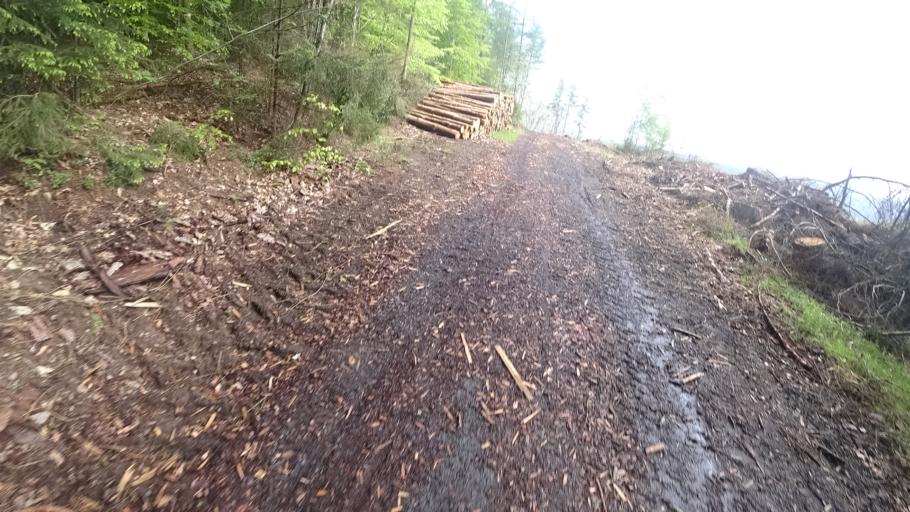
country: DE
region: Rheinland-Pfalz
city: Alsdorf
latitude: 50.7786
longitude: 7.8651
